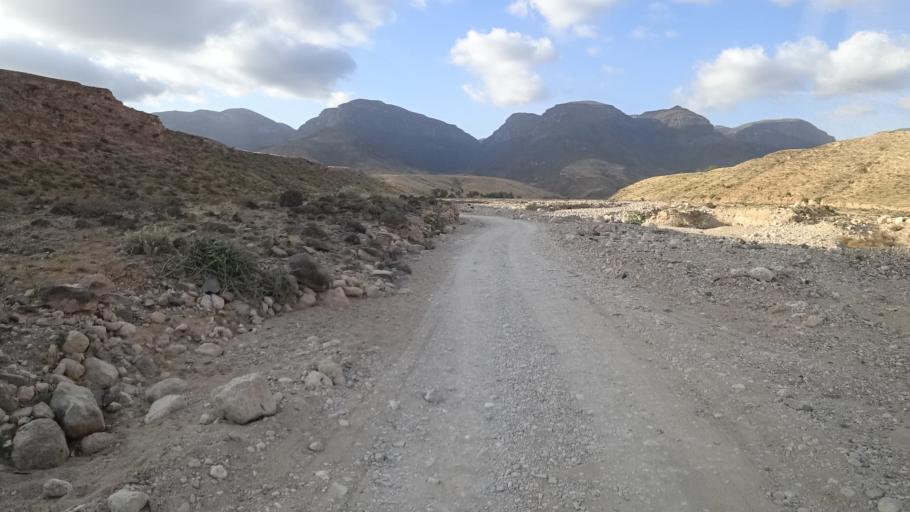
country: OM
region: Zufar
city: Salalah
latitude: 16.9830
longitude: 53.8503
